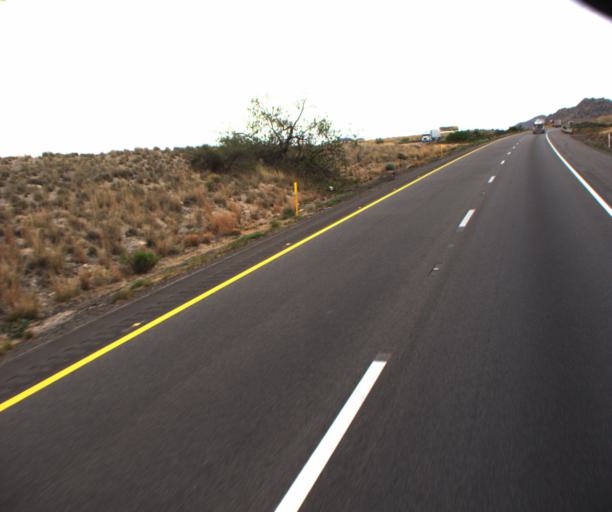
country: US
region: Arizona
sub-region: Cochise County
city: Saint David
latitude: 32.0872
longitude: -110.0426
